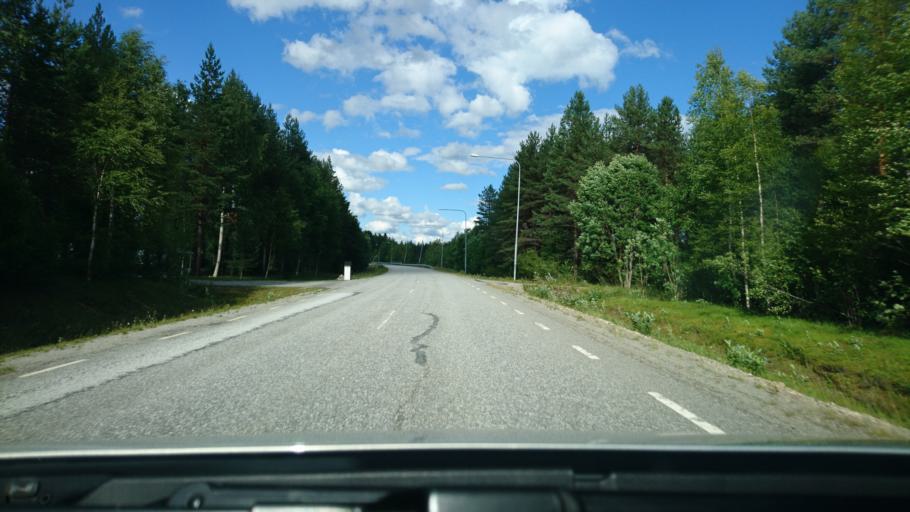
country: SE
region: Vaesterbotten
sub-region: Asele Kommun
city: Asele
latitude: 64.0843
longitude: 17.3202
